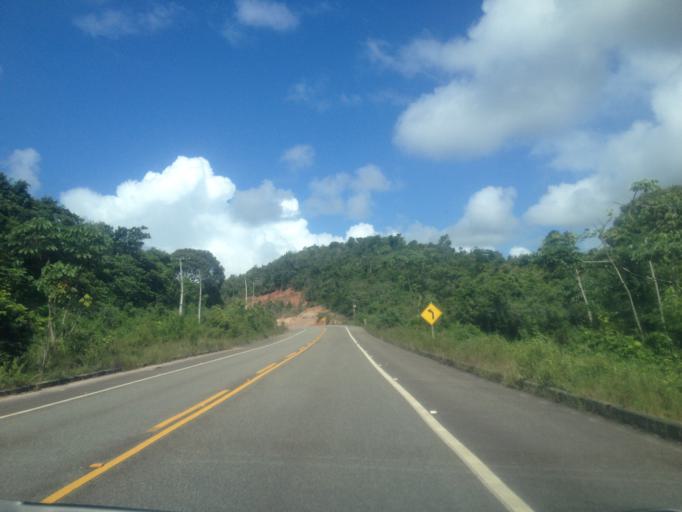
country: BR
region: Sergipe
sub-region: Indiaroba
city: Indiaroba
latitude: -11.4849
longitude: -37.4836
